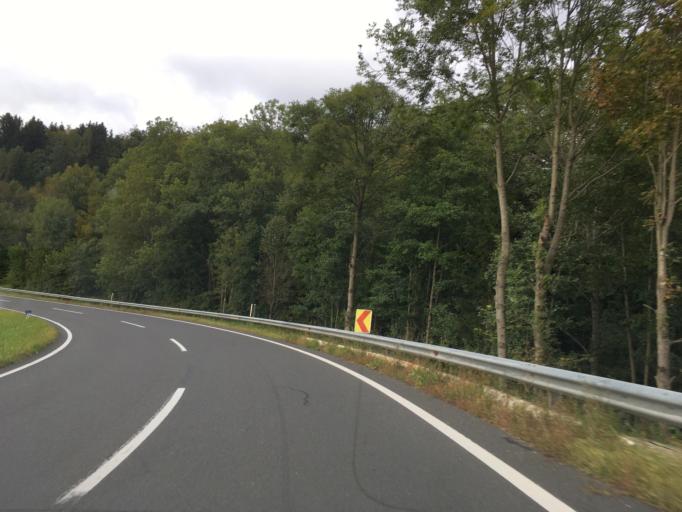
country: AT
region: Styria
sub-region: Politischer Bezirk Hartberg-Fuerstenfeld
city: Pinggau
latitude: 47.4347
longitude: 16.0831
